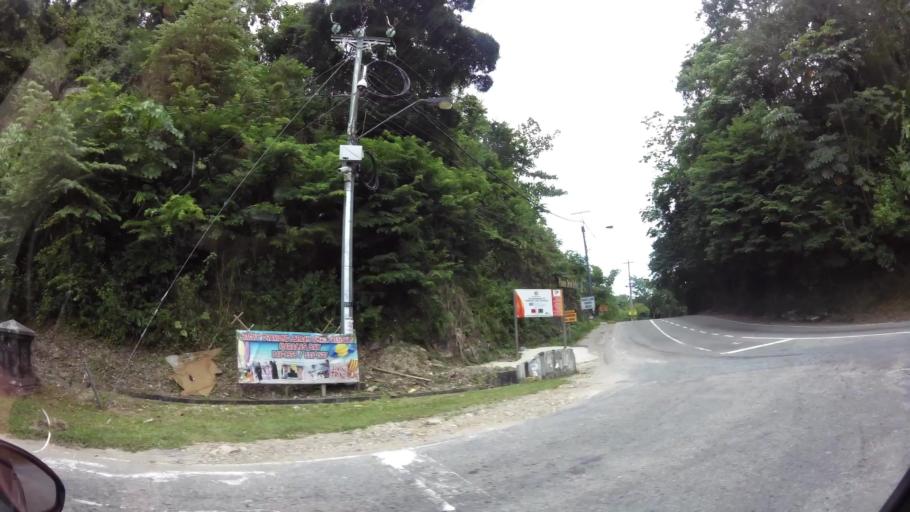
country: TT
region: Diego Martin
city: Petit Valley
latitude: 10.7165
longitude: -61.4961
